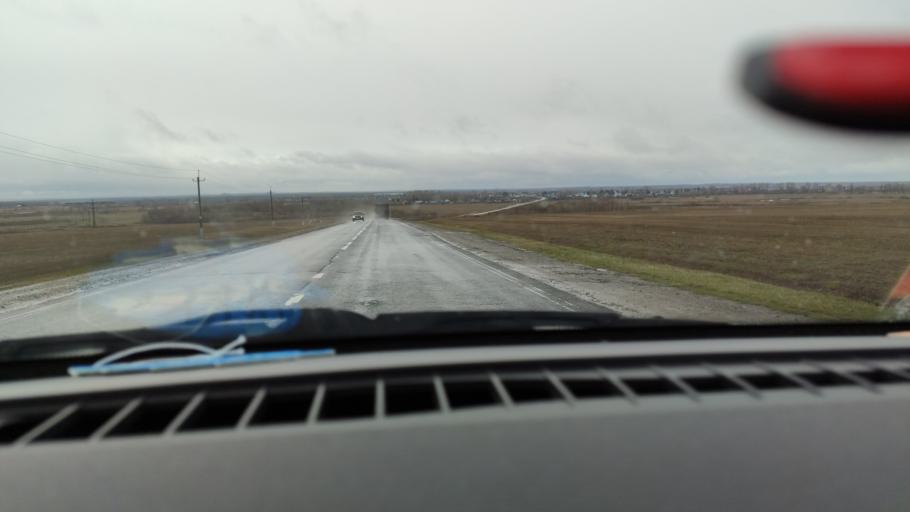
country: RU
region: Tatarstan
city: Nurlat
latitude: 54.5808
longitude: 50.8604
